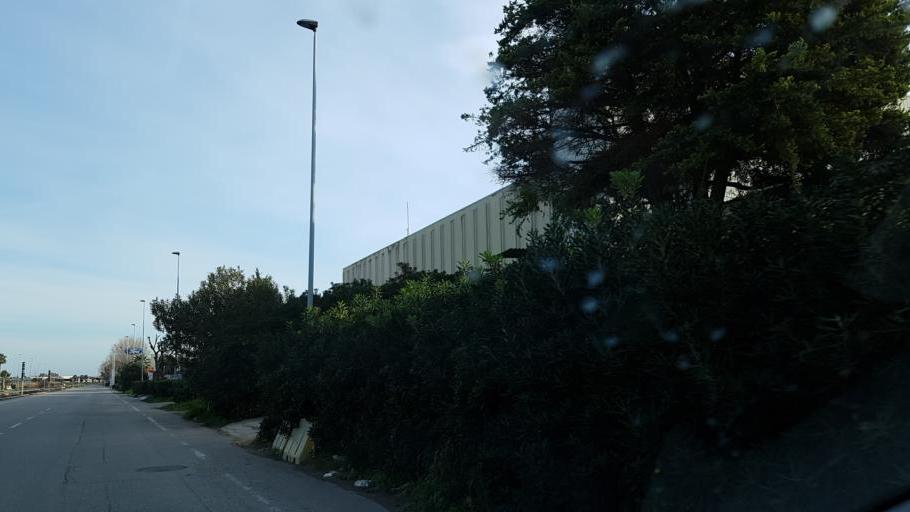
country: IT
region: Apulia
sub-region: Provincia di Brindisi
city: Brindisi
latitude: 40.6323
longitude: 17.9551
